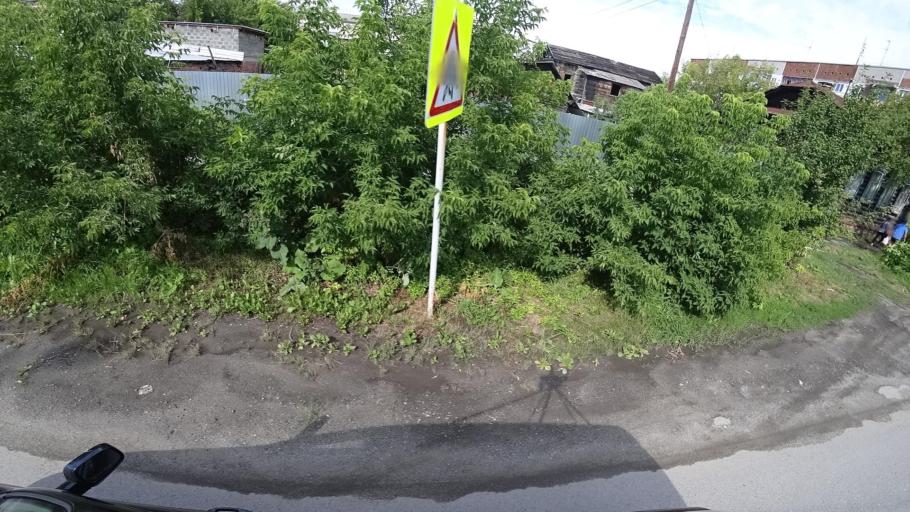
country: RU
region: Sverdlovsk
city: Kamyshlov
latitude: 56.8427
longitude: 62.7151
